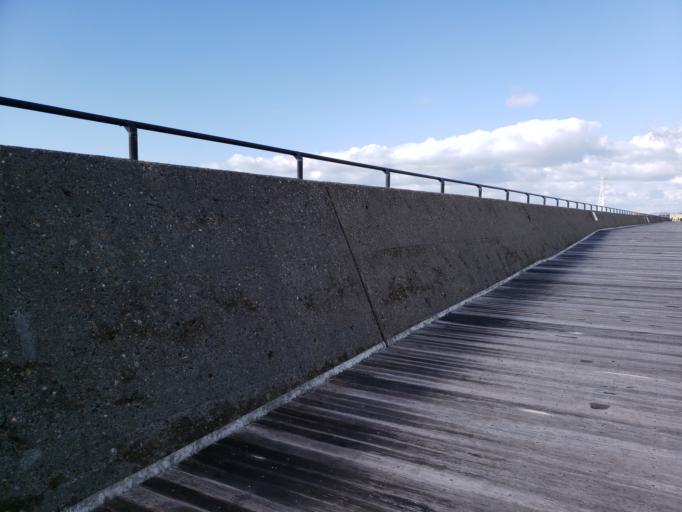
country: JP
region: Hyogo
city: Kakogawacho-honmachi
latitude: 34.7451
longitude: 134.7787
